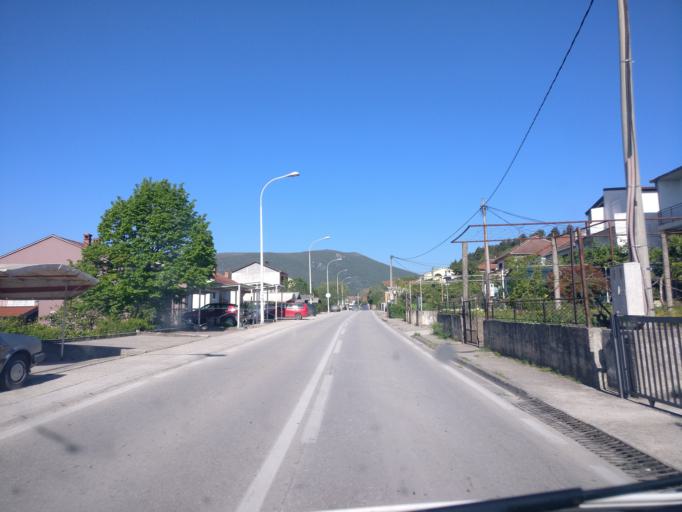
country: BA
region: Federation of Bosnia and Herzegovina
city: Capljina
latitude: 43.1175
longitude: 17.6958
